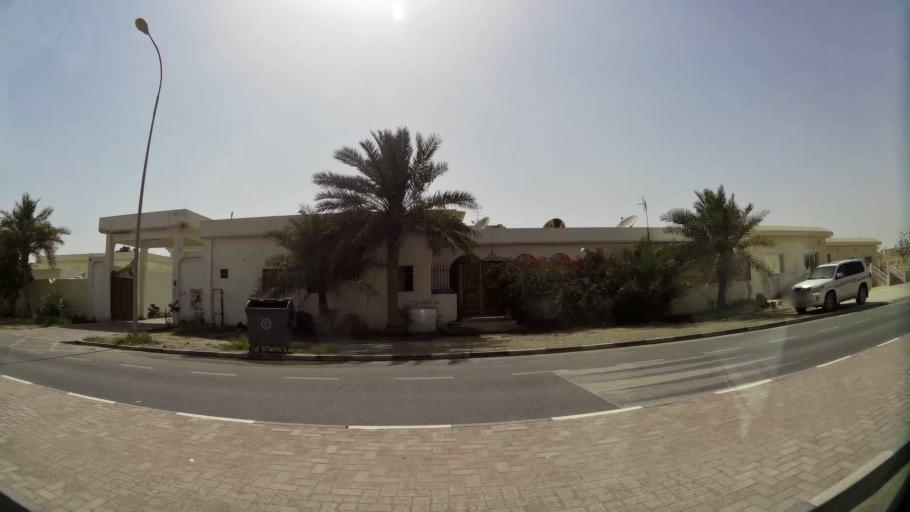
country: QA
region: Baladiyat Umm Salal
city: Umm Salal Muhammad
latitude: 25.3864
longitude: 51.4332
